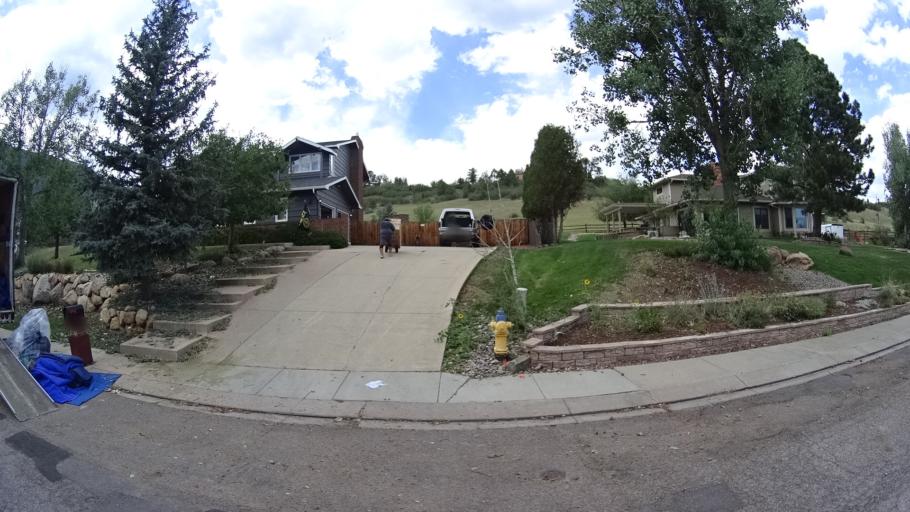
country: US
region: Colorado
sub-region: El Paso County
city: Stratmoor
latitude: 38.7791
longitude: -104.8336
